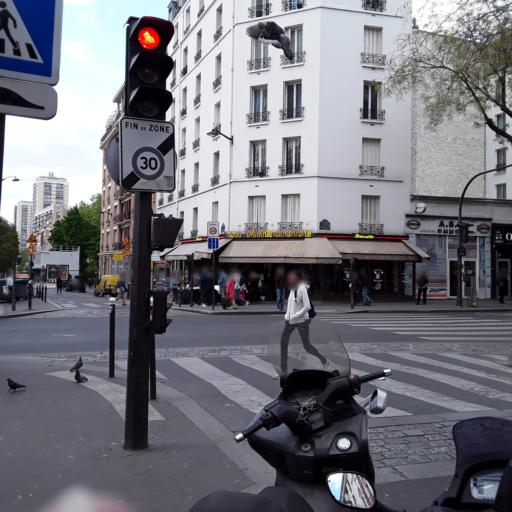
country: FR
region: Ile-de-France
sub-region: Departement du Val-de-Marne
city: Le Kremlin-Bicetre
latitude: 48.8267
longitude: 2.3665
